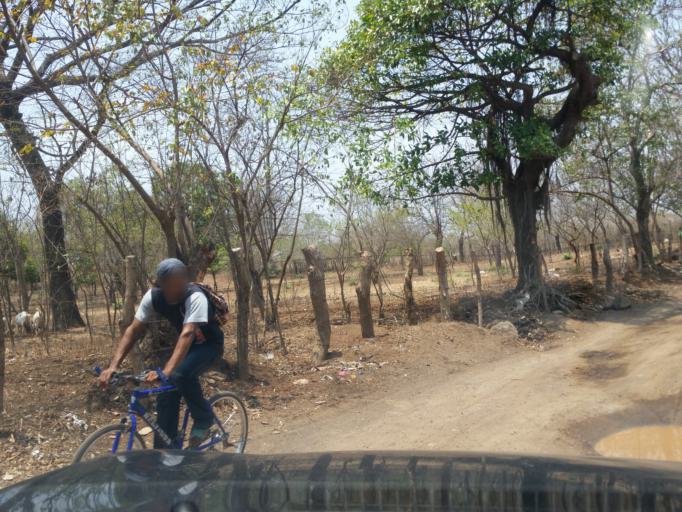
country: NI
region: Granada
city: Granada
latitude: 11.9103
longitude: -85.9653
